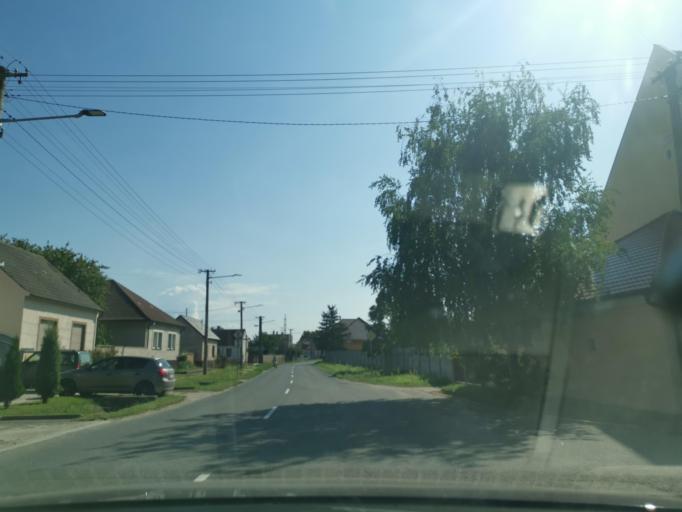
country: SK
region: Trnavsky
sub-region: Okres Senica
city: Senica
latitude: 48.6767
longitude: 17.2572
